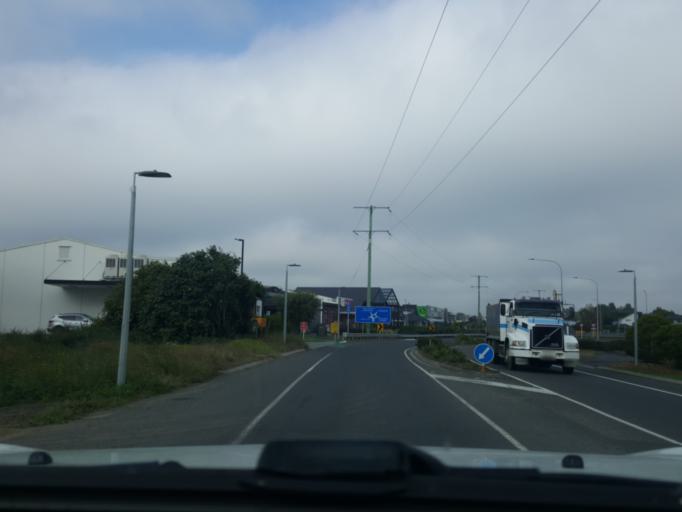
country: NZ
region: Waikato
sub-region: Hamilton City
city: Hamilton
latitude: -37.7486
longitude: 175.2935
